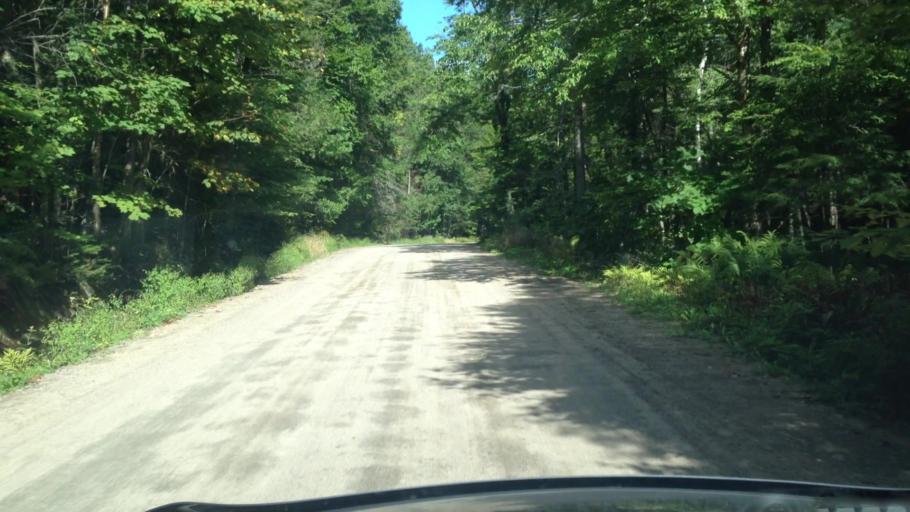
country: CA
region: Quebec
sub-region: Laurentides
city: Mont-Tremblant
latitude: 45.9245
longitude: -74.5829
